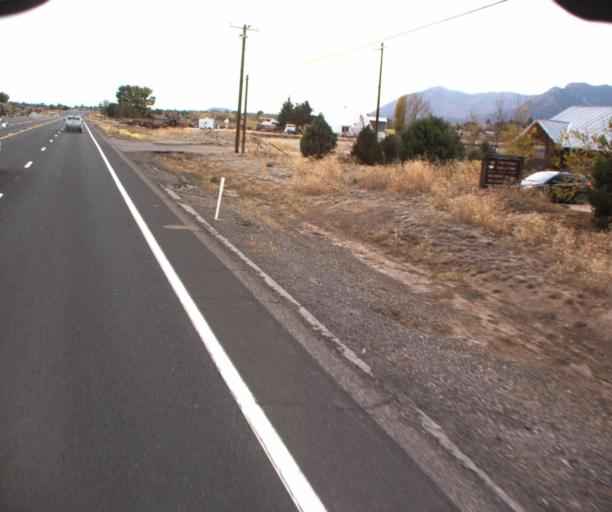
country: US
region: Arizona
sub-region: Coconino County
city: Flagstaff
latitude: 35.3123
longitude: -111.5427
